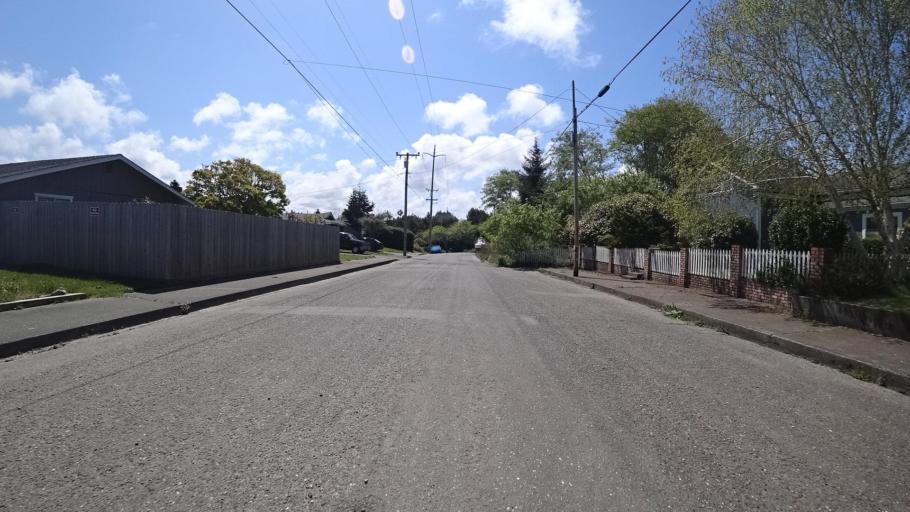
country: US
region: California
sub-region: Humboldt County
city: Bayview
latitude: 40.7748
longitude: -124.1716
